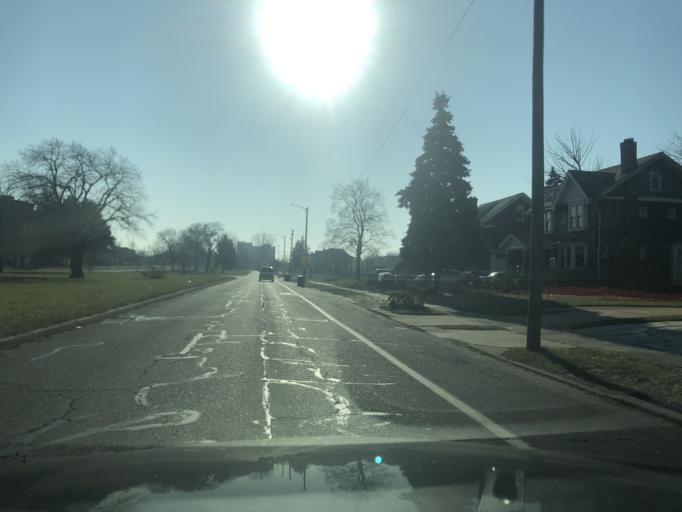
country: US
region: Michigan
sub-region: Wayne County
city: Highland Park
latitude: 42.3512
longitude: -83.1107
